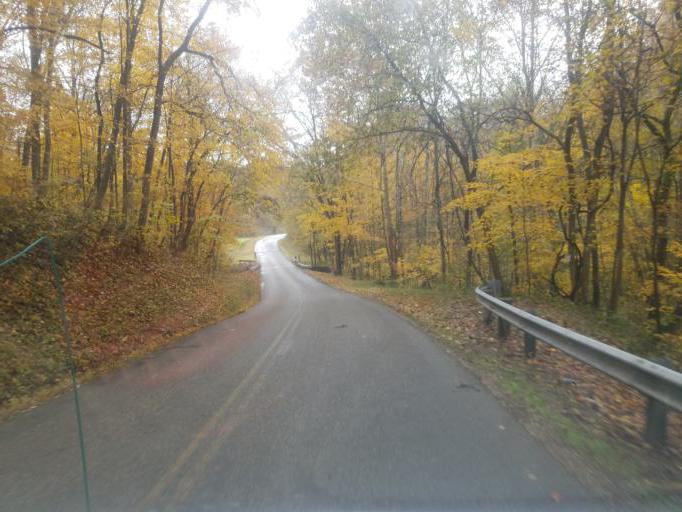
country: US
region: Ohio
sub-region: Washington County
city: Beverly
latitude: 39.5504
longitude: -81.6617
